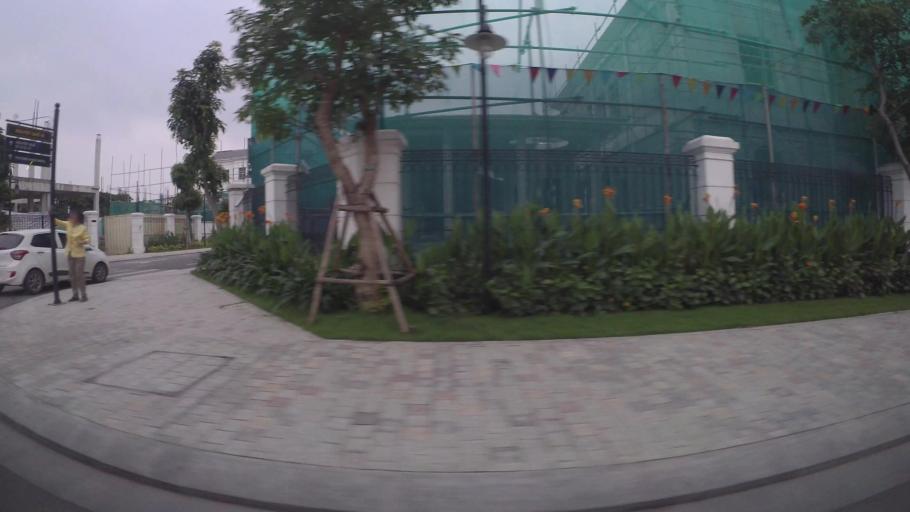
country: VN
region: Ha Noi
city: Trau Quy
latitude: 21.0457
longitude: 105.9068
